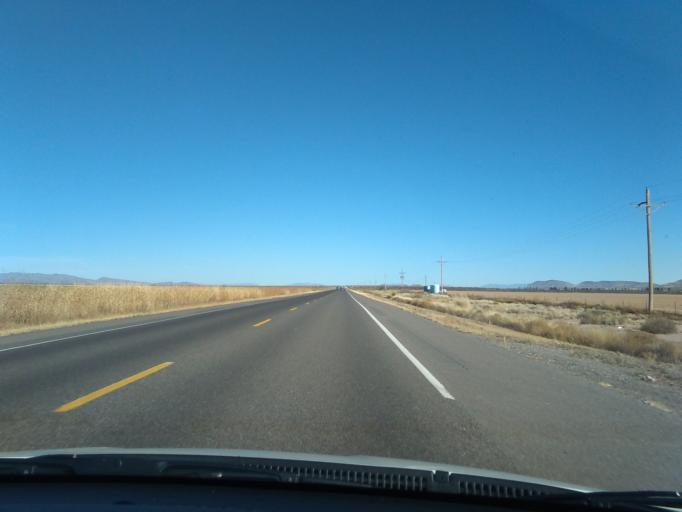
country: US
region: New Mexico
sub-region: Dona Ana County
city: Hatch
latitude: 32.5998
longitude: -107.3299
